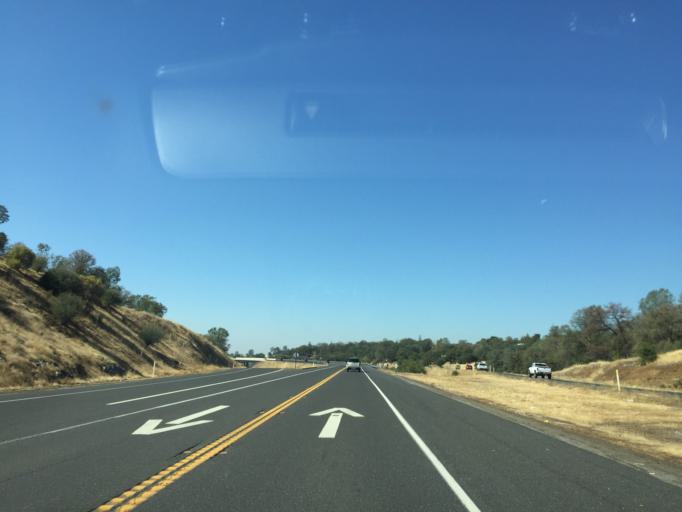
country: US
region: California
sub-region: Tuolumne County
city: East Sonora
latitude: 37.9777
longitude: -120.3521
